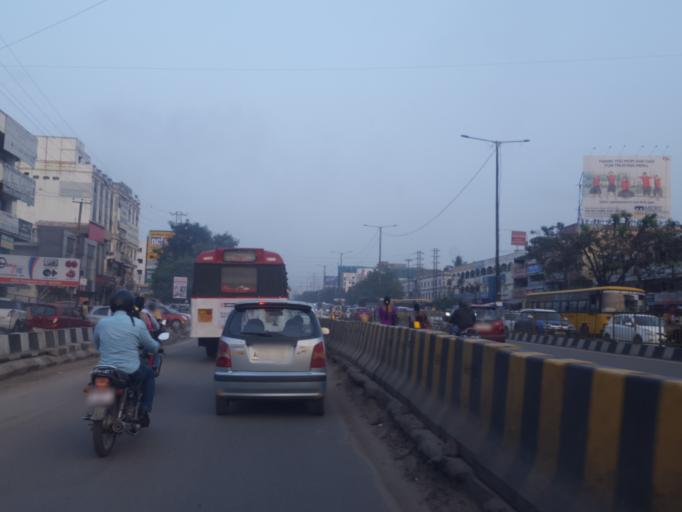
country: IN
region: Telangana
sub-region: Medak
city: Serilingampalle
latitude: 17.4952
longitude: 78.3175
